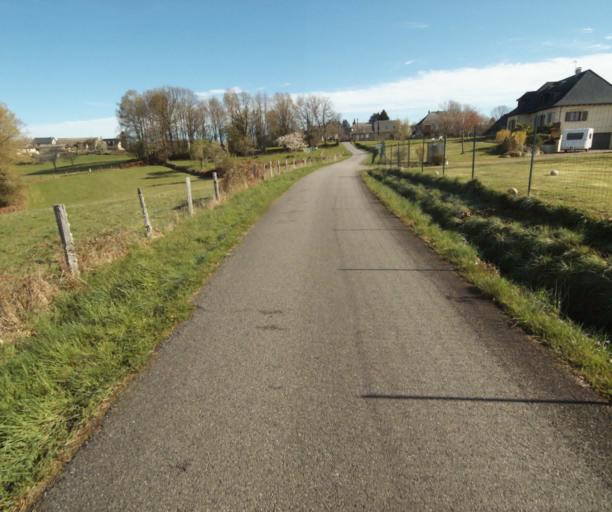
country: FR
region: Limousin
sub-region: Departement de la Correze
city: Laguenne
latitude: 45.2644
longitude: 1.8562
